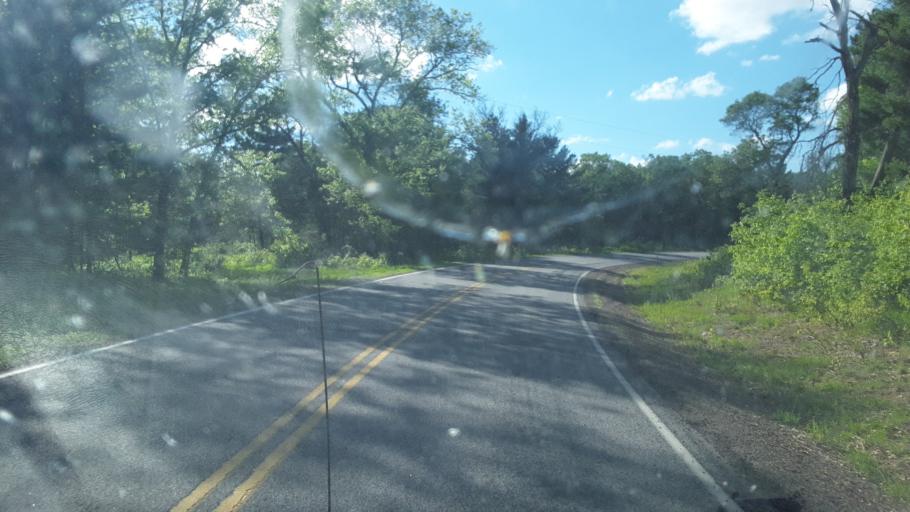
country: US
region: Wisconsin
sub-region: Wood County
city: Nekoosa
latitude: 44.3219
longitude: -90.1297
